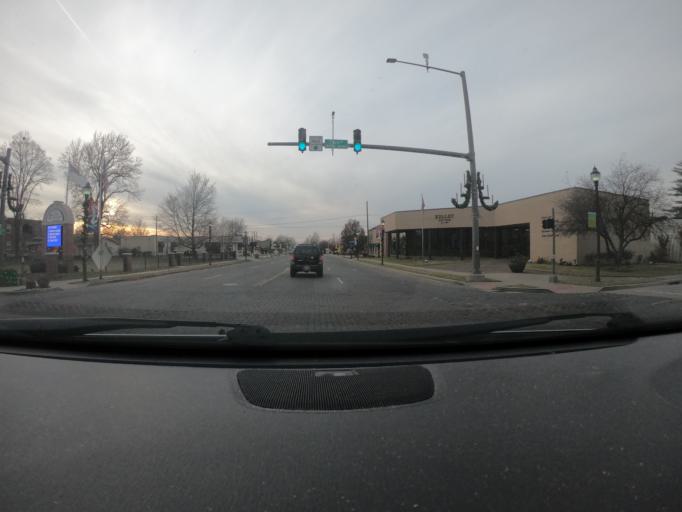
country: US
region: Arkansas
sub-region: Benton County
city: Rogers
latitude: 36.3332
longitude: -94.1186
